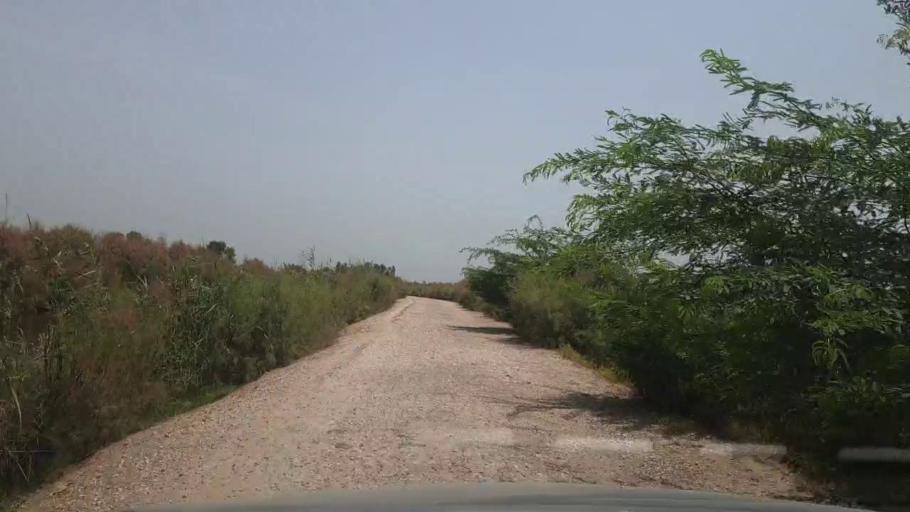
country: PK
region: Sindh
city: Garhi Yasin
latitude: 27.9236
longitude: 68.3785
